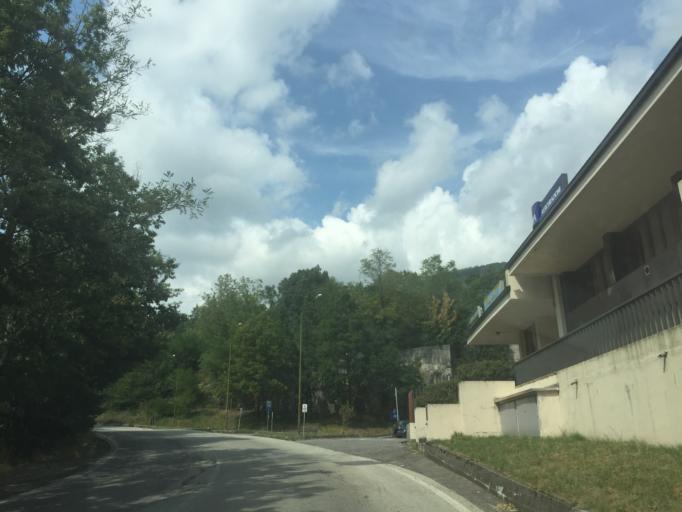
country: IT
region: Tuscany
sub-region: Provincia di Pistoia
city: San Marcello Pistoiese
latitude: 44.0493
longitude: 10.8071
